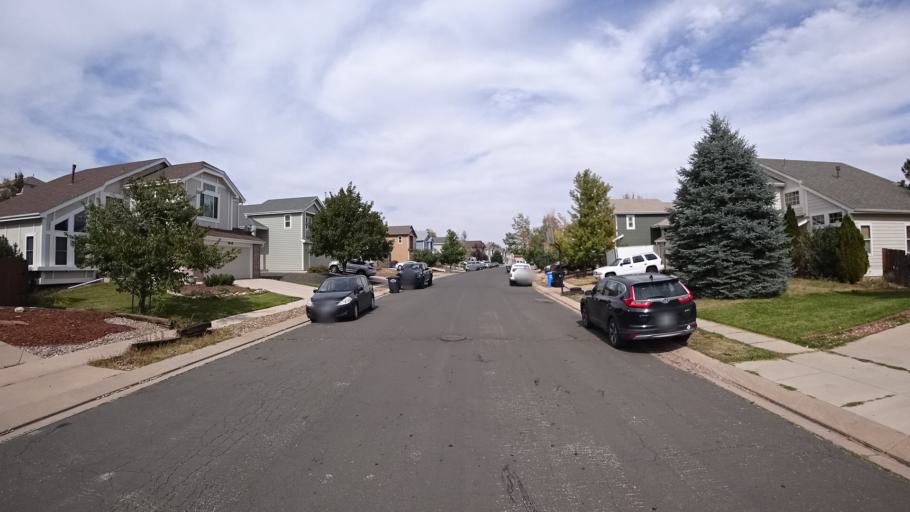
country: US
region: Colorado
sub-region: El Paso County
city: Cimarron Hills
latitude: 38.9035
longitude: -104.7165
